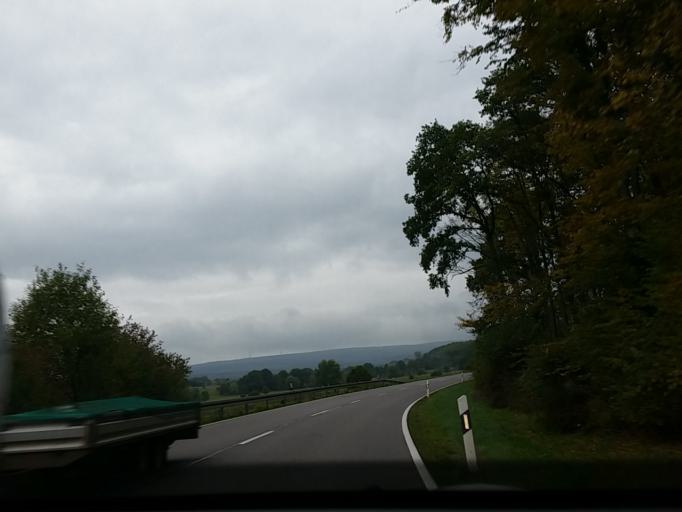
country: DE
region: Saarland
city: Weiskirchen
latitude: 49.5126
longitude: 6.8265
